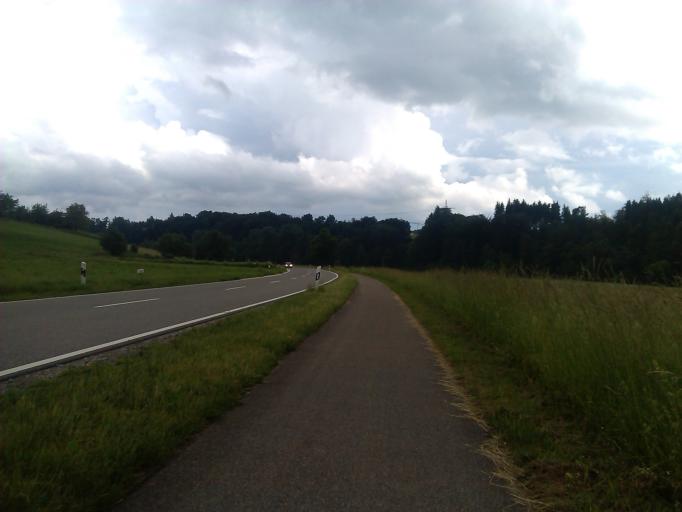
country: DE
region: Baden-Wuerttemberg
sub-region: Regierungsbezirk Stuttgart
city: Abtsgmund
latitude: 48.8985
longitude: 9.9915
